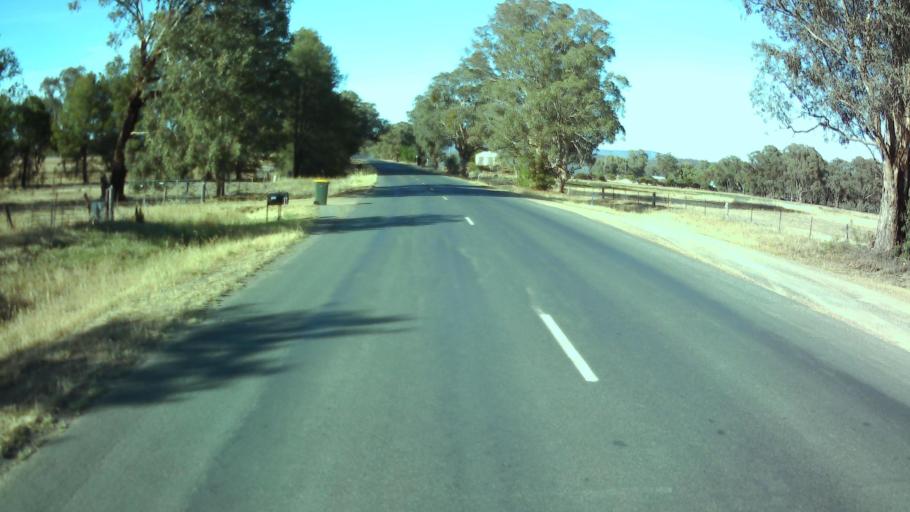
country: AU
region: New South Wales
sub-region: Weddin
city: Grenfell
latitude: -33.9034
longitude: 148.1495
